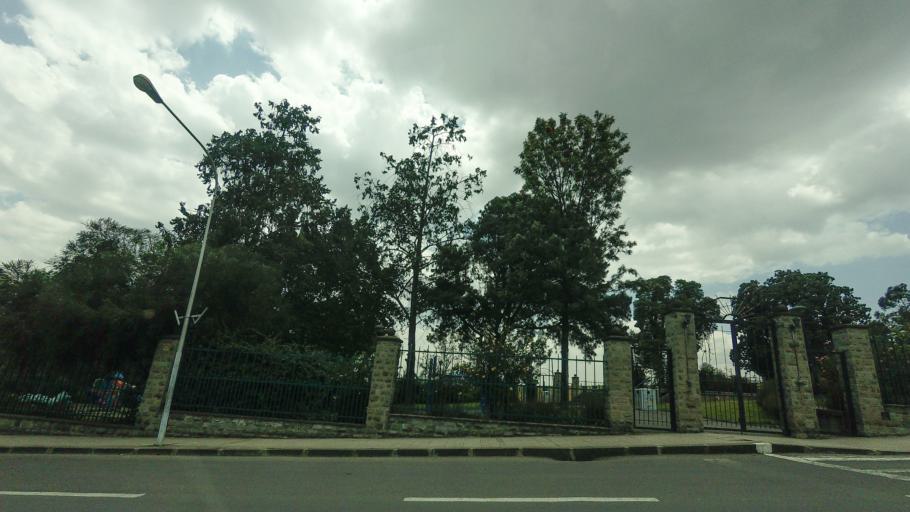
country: ET
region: Adis Abeba
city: Addis Ababa
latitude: 9.0205
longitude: 38.7640
